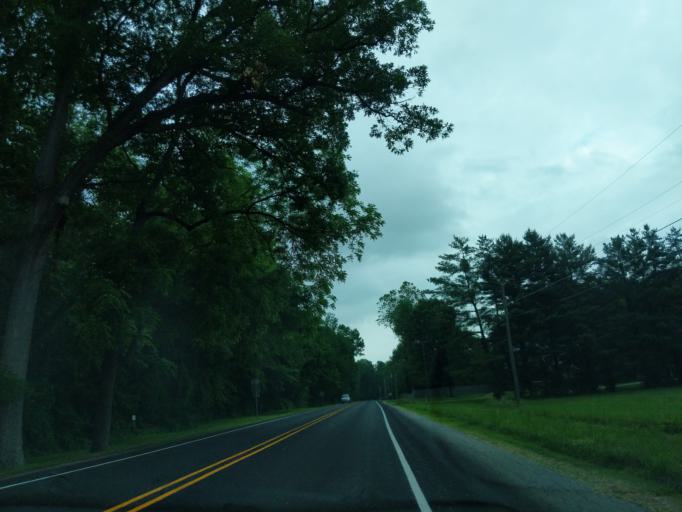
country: US
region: Indiana
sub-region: Madison County
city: Chesterfield
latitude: 40.0924
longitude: -85.6233
